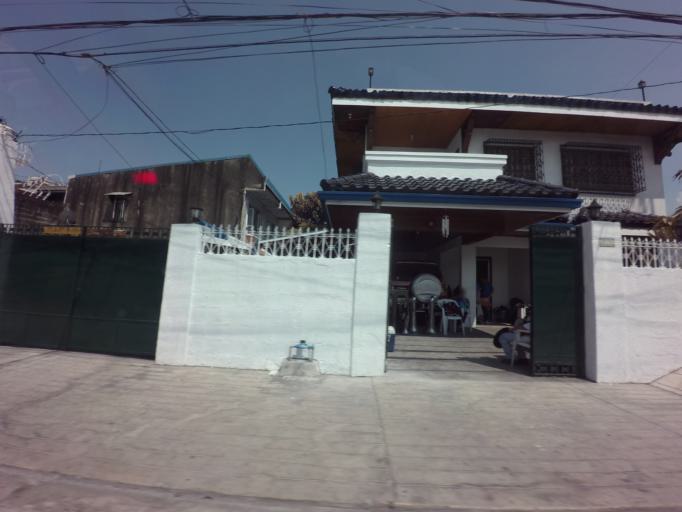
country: PH
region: Metro Manila
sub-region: Makati City
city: Makati City
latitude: 14.5716
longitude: 121.0115
